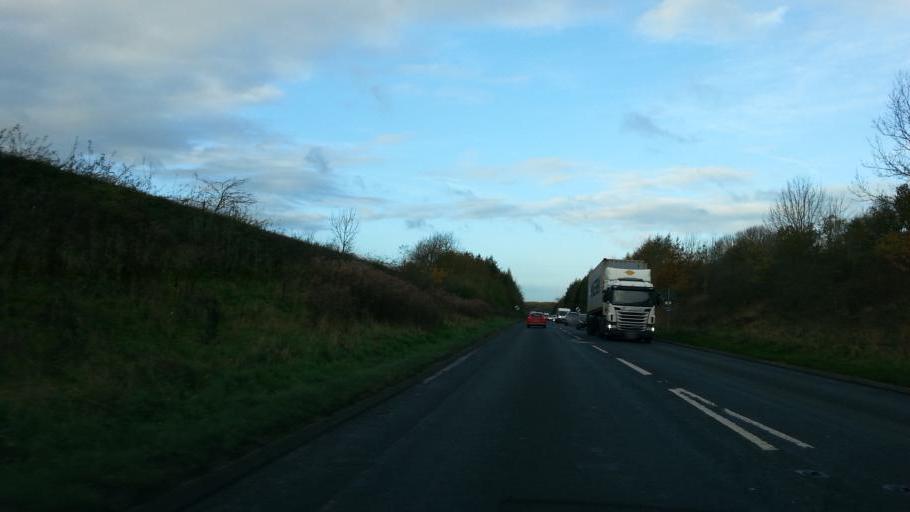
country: GB
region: England
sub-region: Leicestershire
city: Coalville
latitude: 52.7341
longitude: -1.4184
